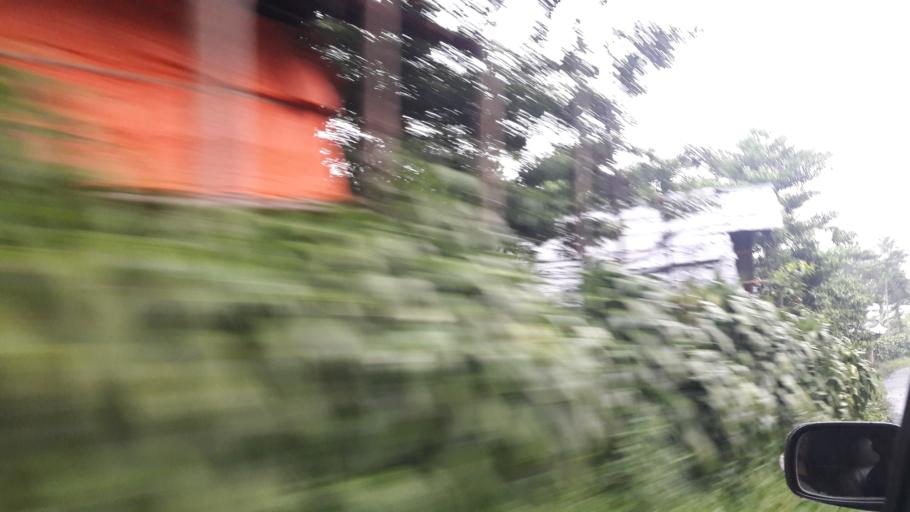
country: ID
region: West Java
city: Cipeundeuy
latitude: -6.6515
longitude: 106.5198
